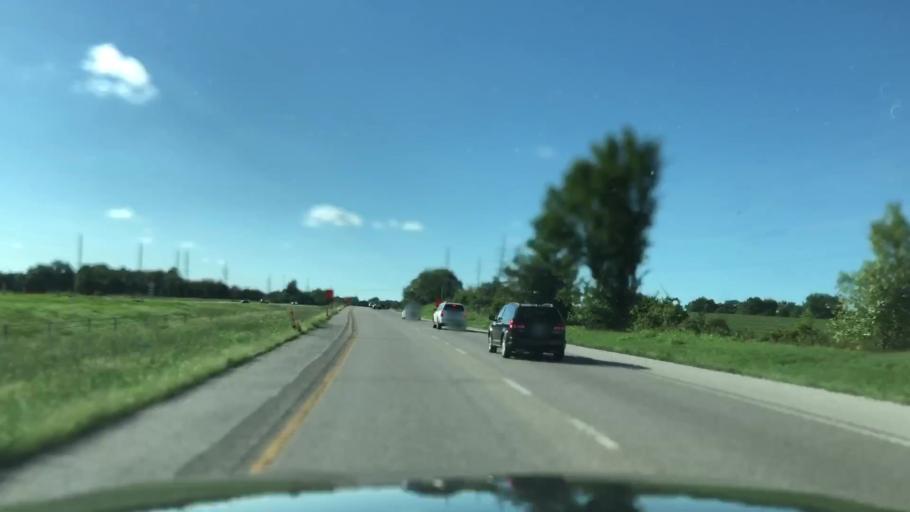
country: US
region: Missouri
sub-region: Saint Charles County
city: Wentzville
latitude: 38.8611
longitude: -90.8771
